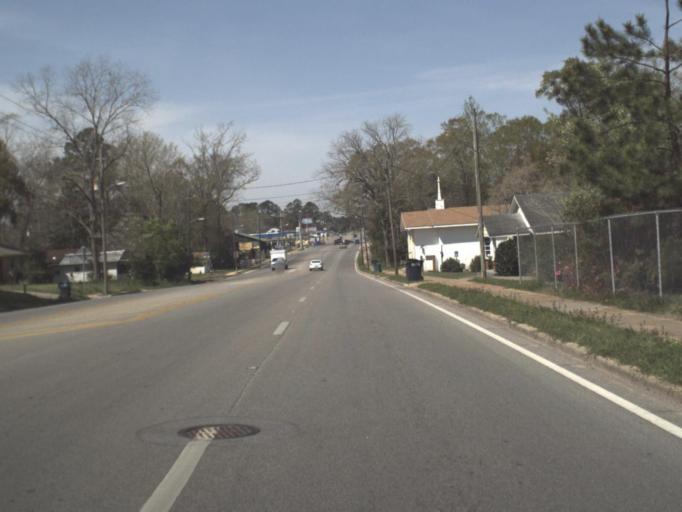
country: US
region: Florida
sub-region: Holmes County
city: Bonifay
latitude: 30.7880
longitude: -85.6758
